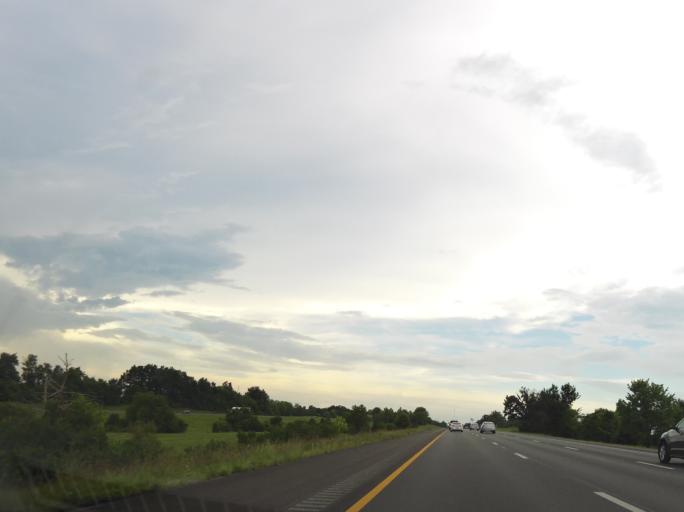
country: US
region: Kentucky
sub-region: Madison County
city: Richmond
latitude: 37.8173
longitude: -84.3233
